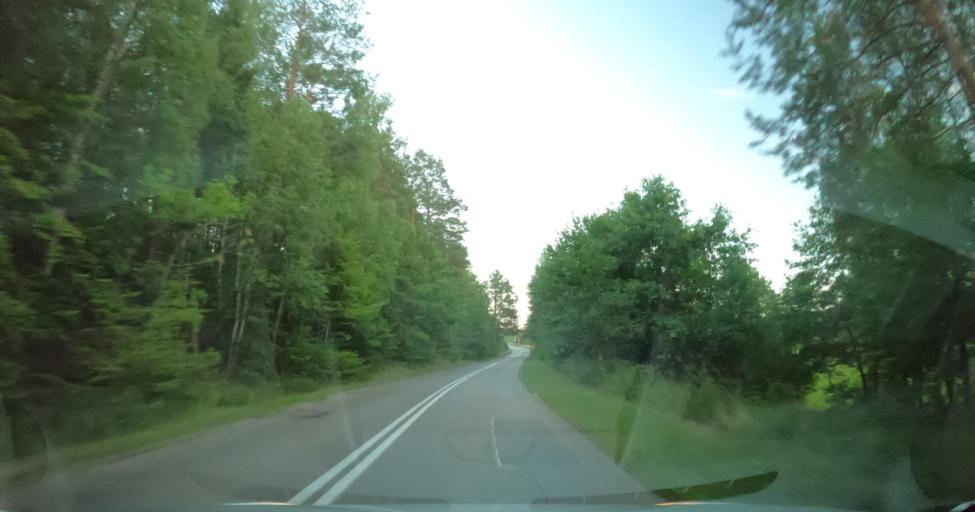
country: PL
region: Pomeranian Voivodeship
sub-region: Powiat wejherowski
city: Linia
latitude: 54.4594
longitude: 18.0018
